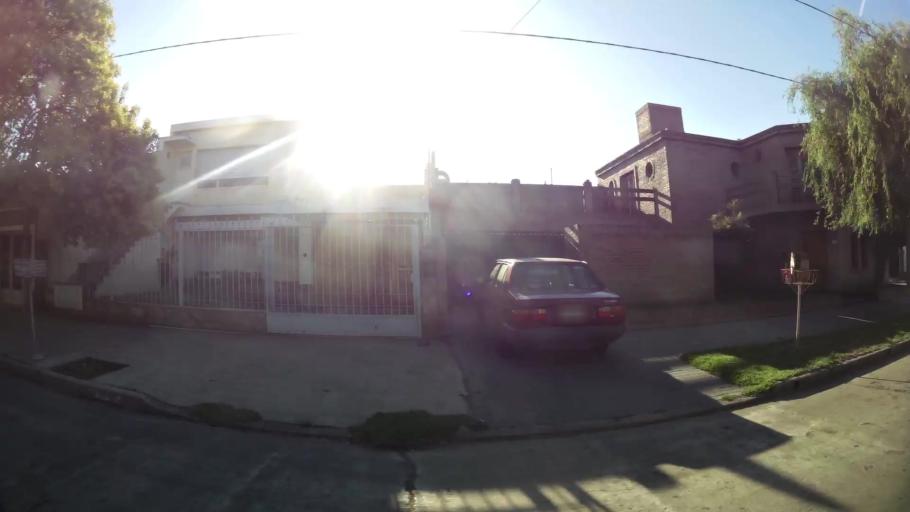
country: AR
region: Cordoba
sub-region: Departamento de Capital
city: Cordoba
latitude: -31.3776
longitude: -64.1798
